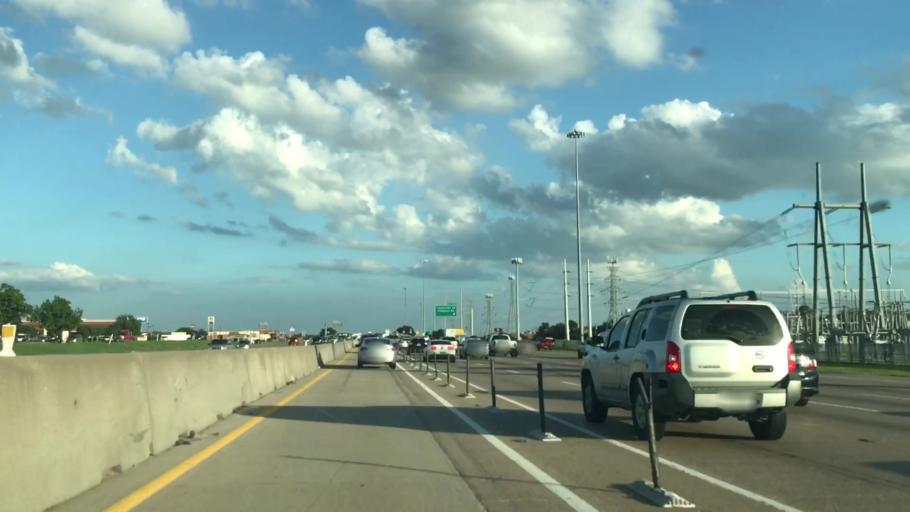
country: US
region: Texas
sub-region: Dallas County
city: Garland
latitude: 32.8593
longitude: -96.6540
